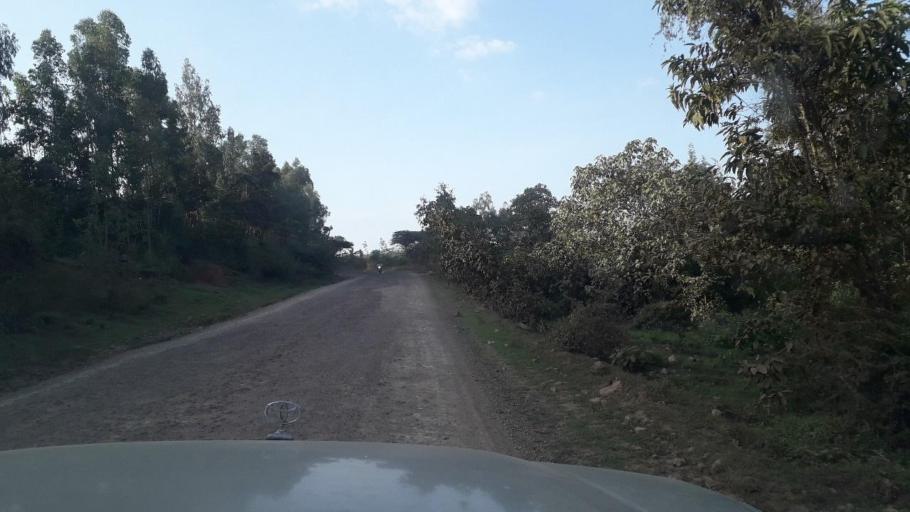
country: ET
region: Oromiya
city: Jima
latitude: 7.5870
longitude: 36.8572
